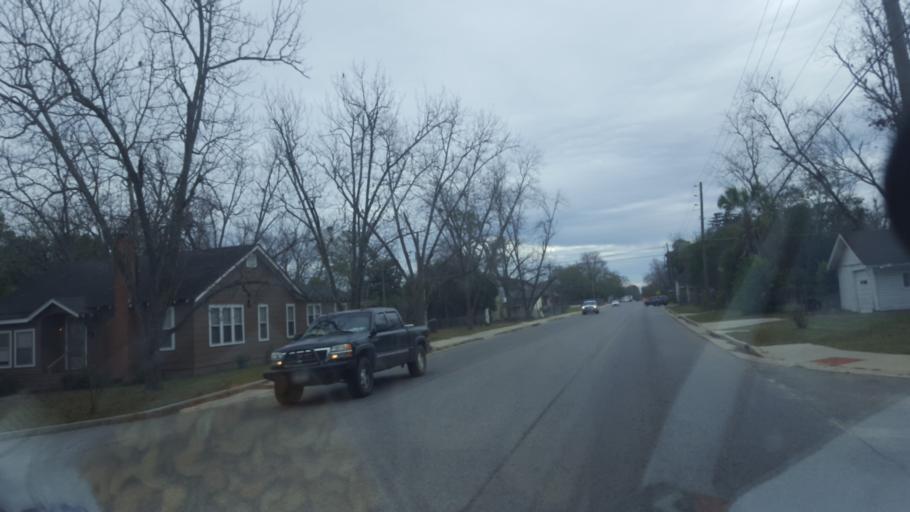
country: US
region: Georgia
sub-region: Ben Hill County
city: Fitzgerald
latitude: 31.7206
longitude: -83.2599
